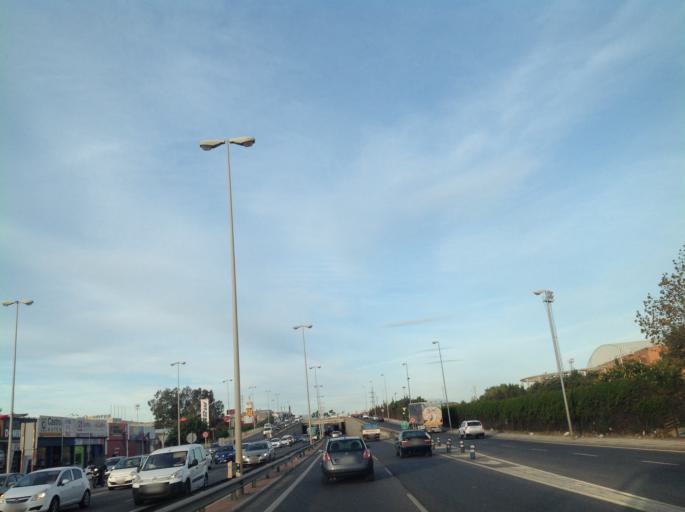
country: ES
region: Andalusia
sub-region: Provincia de Malaga
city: Malaga
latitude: 36.7141
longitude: -4.4790
